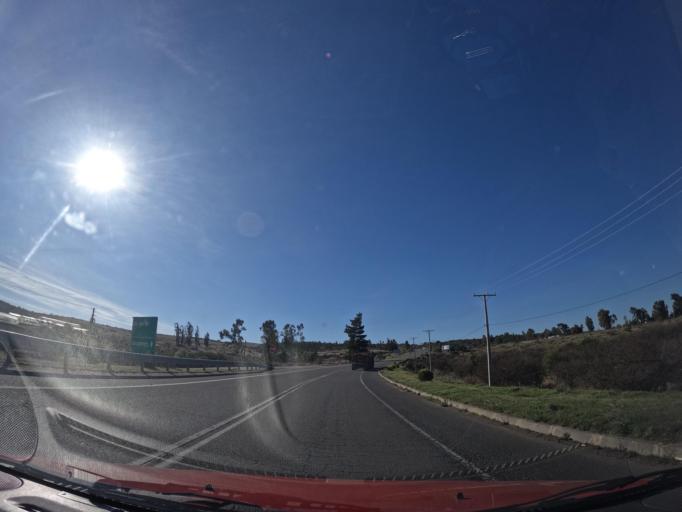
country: CL
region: Maule
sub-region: Provincia de Cauquenes
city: Cauquenes
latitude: -35.9434
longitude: -72.2000
